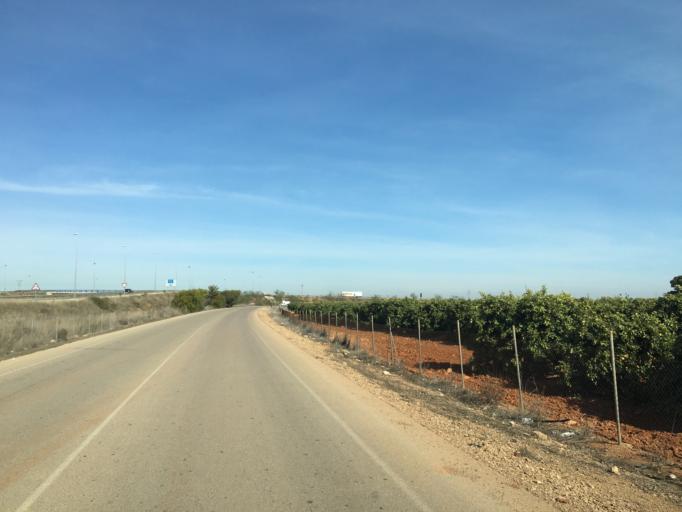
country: ES
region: Murcia
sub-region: Murcia
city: Cartagena
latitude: 37.6606
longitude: -1.0243
